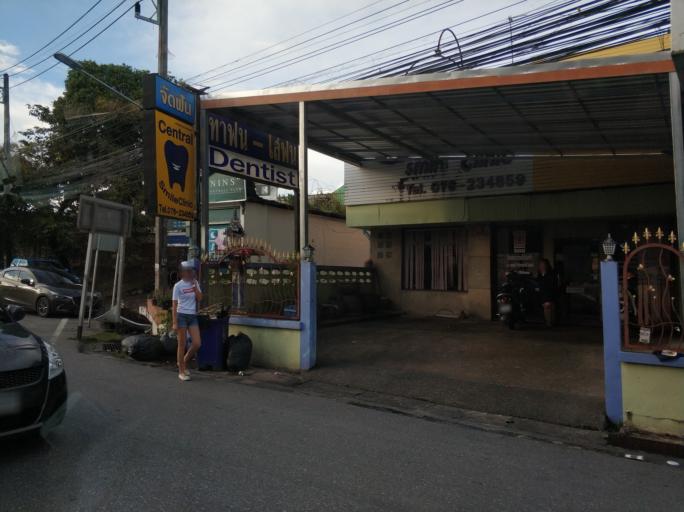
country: TH
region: Phuket
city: Wichit
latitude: 7.8877
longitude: 98.3722
